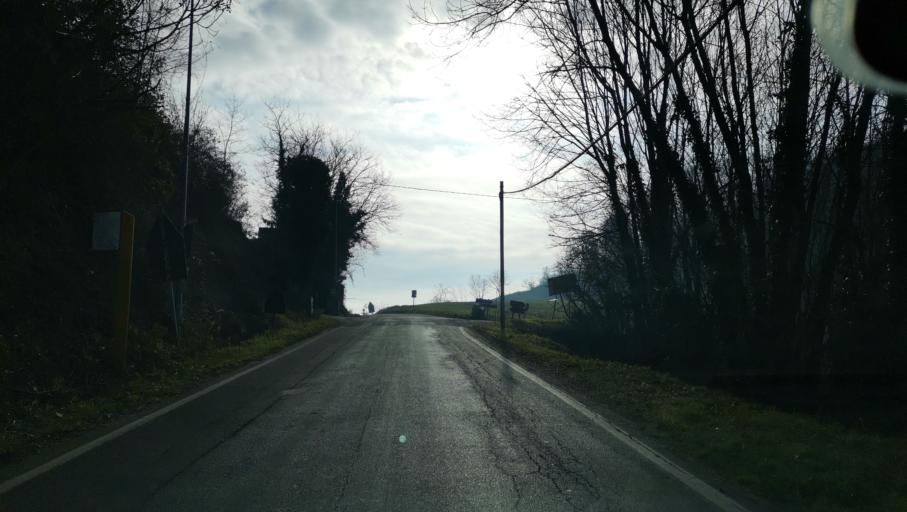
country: IT
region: Piedmont
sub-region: Provincia di Torino
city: Sciolze
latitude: 45.0964
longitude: 7.8900
